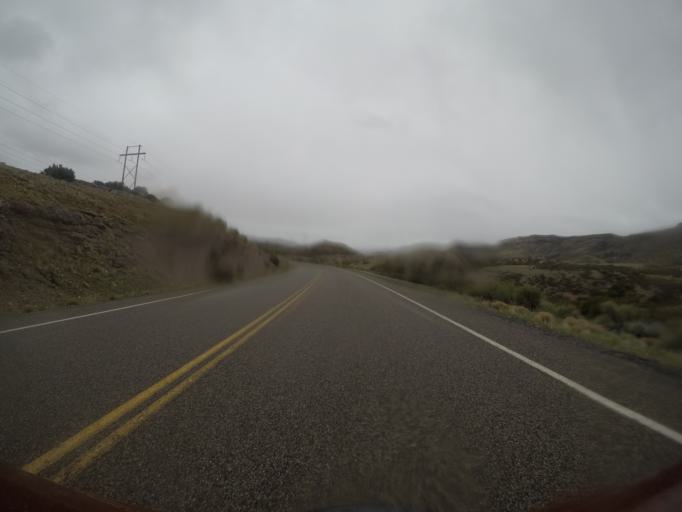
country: US
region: Wyoming
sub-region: Big Horn County
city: Lovell
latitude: 45.0233
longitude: -108.2697
